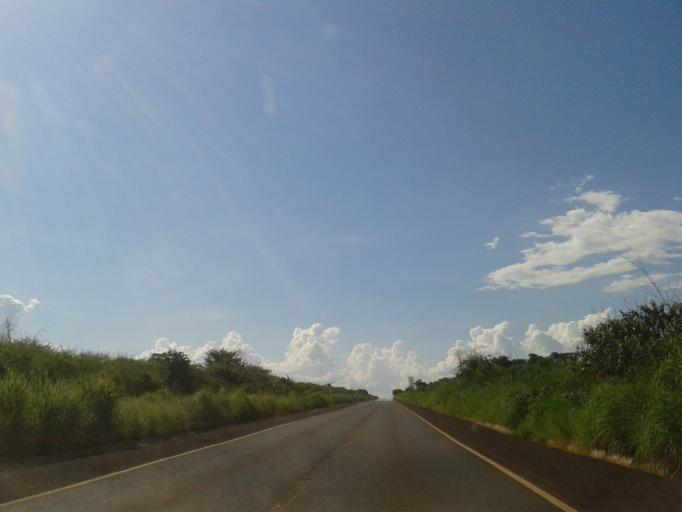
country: BR
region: Minas Gerais
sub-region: Santa Vitoria
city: Santa Vitoria
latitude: -19.0534
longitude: -50.3966
